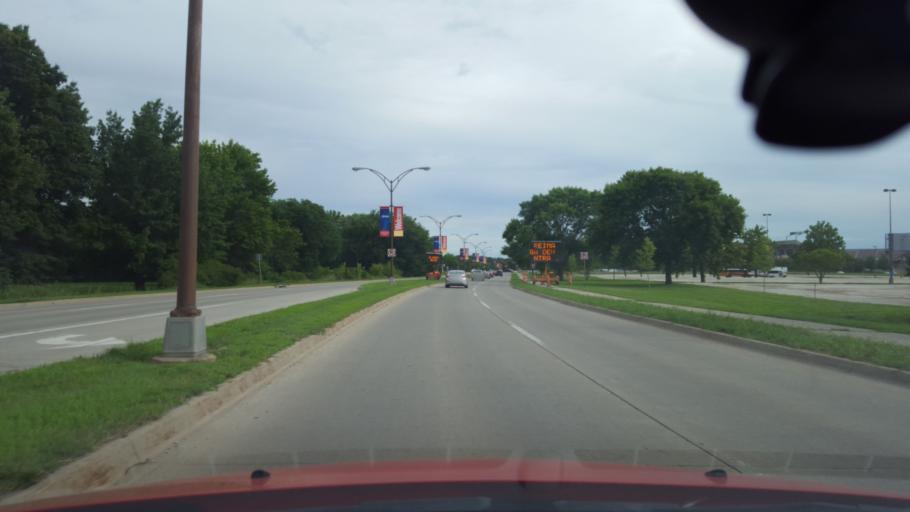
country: US
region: Iowa
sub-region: Story County
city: Ames
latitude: 42.0196
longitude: -93.6325
